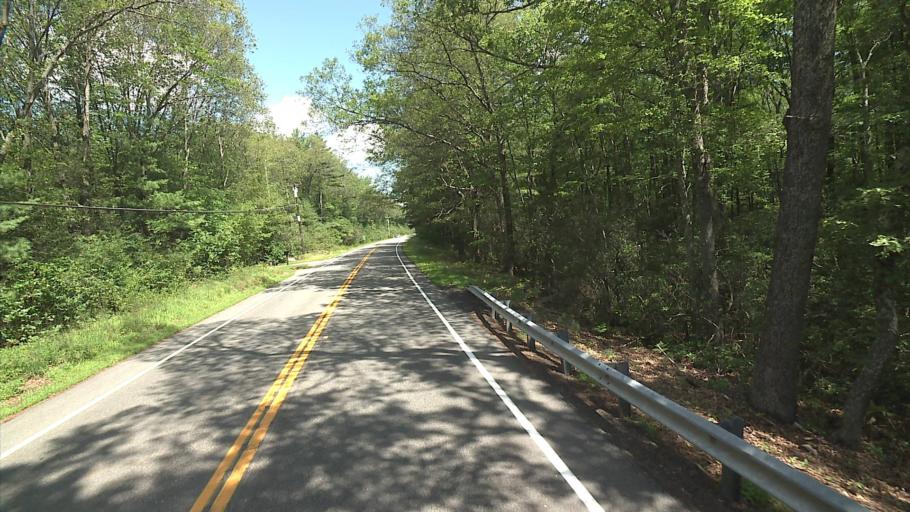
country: US
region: Massachusetts
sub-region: Worcester County
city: Southbridge
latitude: 42.0080
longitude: -72.0814
